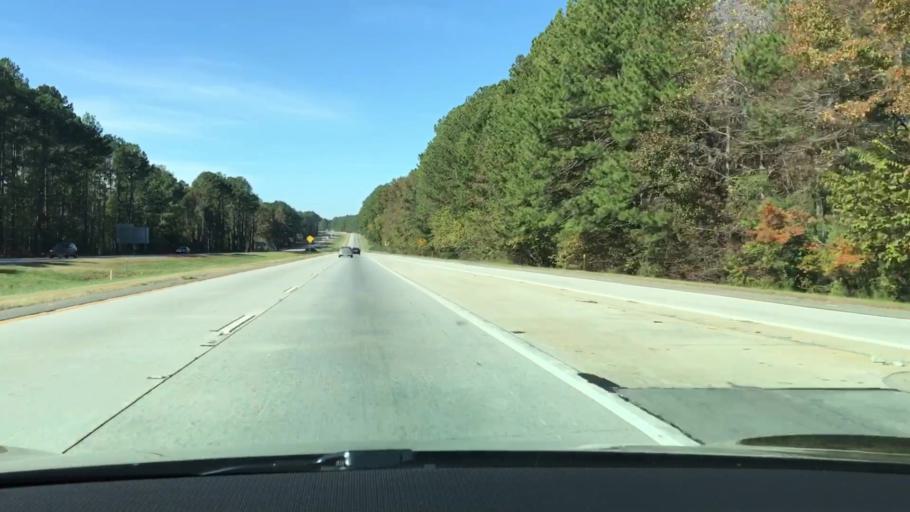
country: US
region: Georgia
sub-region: Taliaferro County
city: Crawfordville
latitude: 33.5301
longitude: -82.9149
